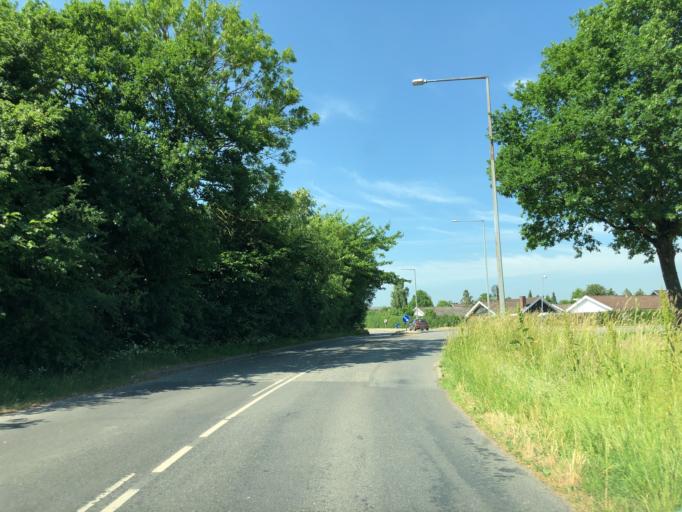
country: DK
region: South Denmark
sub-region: Kolding Kommune
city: Kolding
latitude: 55.5165
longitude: 9.4850
